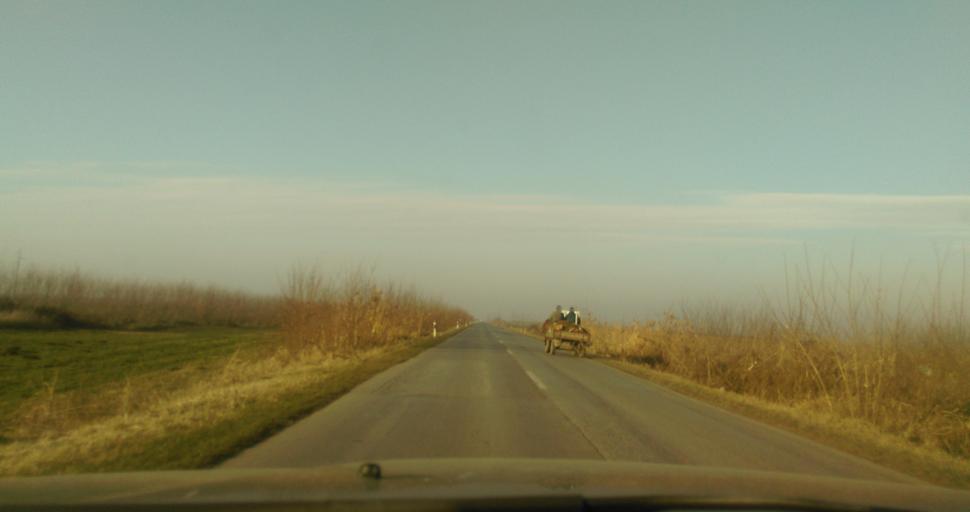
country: RS
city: Curug
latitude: 45.4772
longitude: 20.0427
